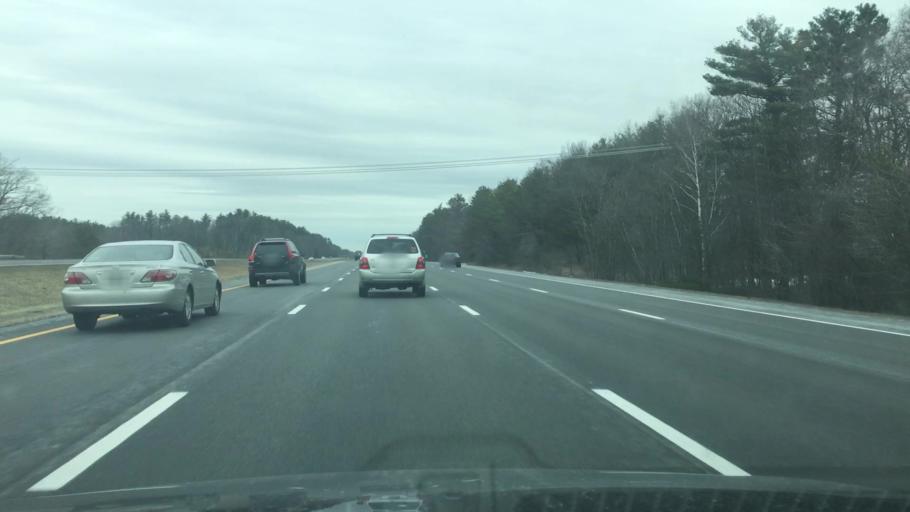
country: US
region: Massachusetts
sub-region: Essex County
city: Boxford
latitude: 42.7248
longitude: -70.9568
